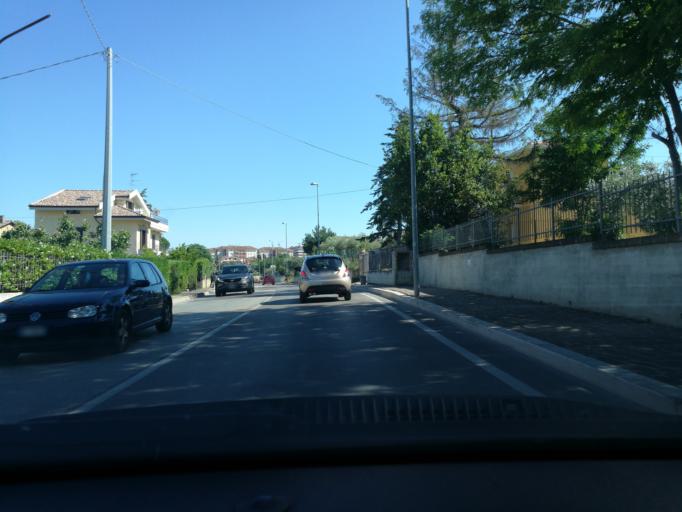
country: IT
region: Abruzzo
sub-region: Provincia di Chieti
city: Vasto
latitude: 42.1323
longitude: 14.6992
